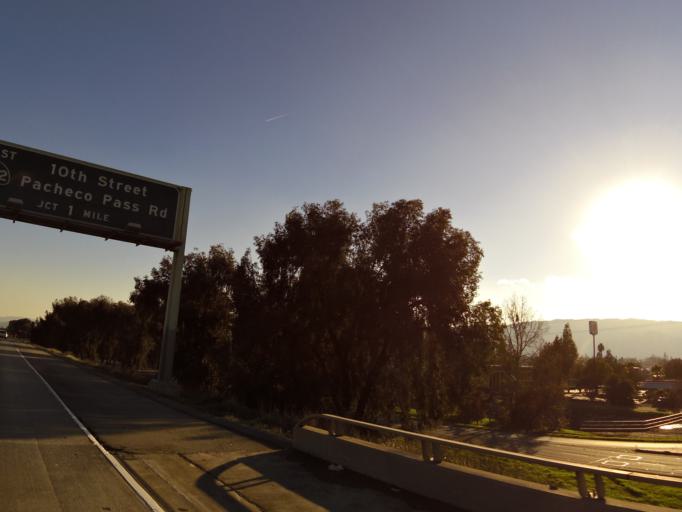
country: US
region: California
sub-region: Santa Clara County
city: Gilroy
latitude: 37.0223
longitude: -121.5668
